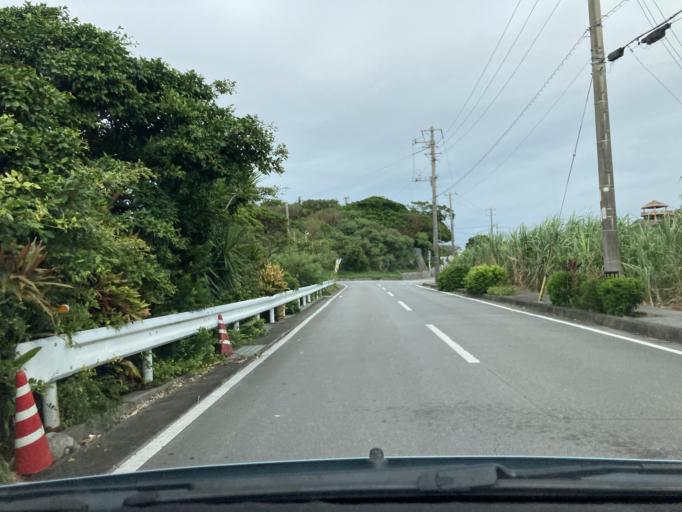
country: JP
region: Okinawa
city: Tomigusuku
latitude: 26.1562
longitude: 127.6998
